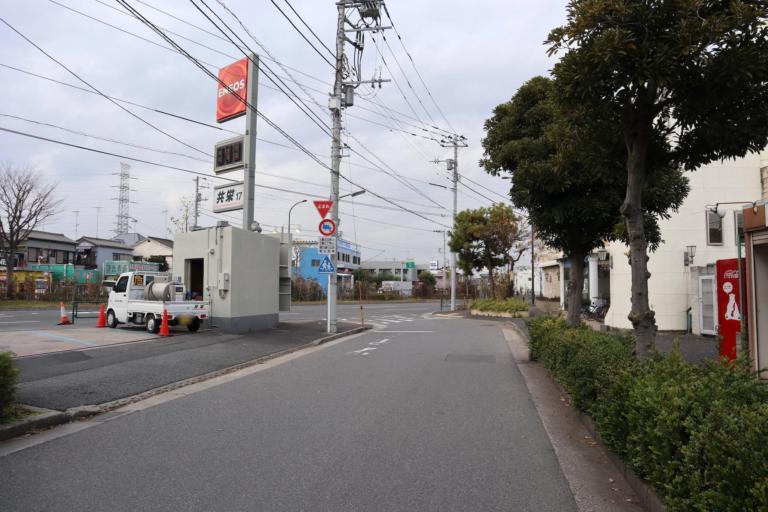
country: JP
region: Tokyo
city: Urayasu
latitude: 35.6993
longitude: 139.8822
